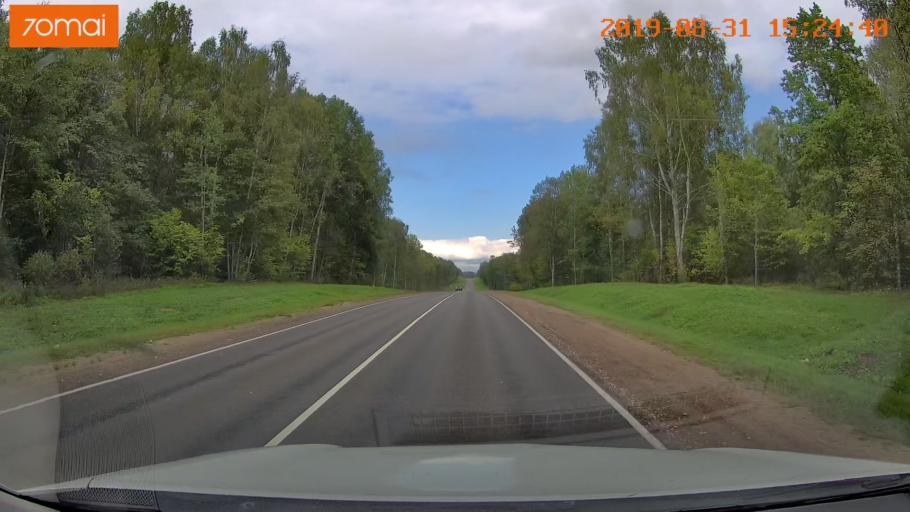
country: RU
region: Kaluga
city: Baryatino
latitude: 54.5308
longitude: 34.5081
